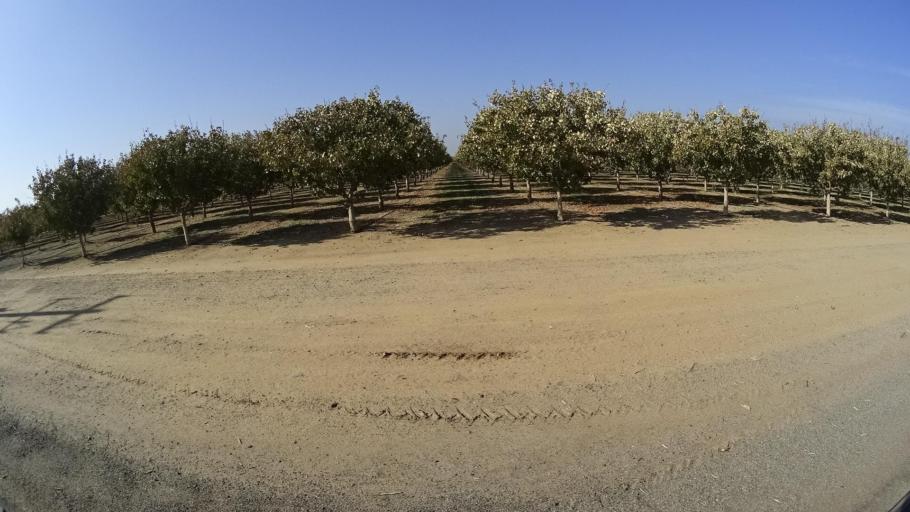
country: US
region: California
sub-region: Kern County
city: McFarland
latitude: 35.6393
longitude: -119.1689
